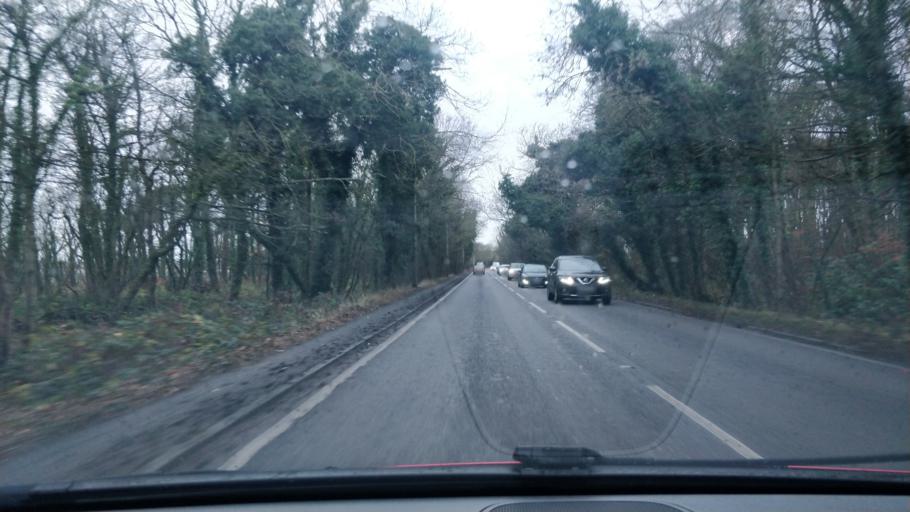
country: GB
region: England
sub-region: Sefton
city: Ince Blundell
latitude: 53.5185
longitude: -3.0241
